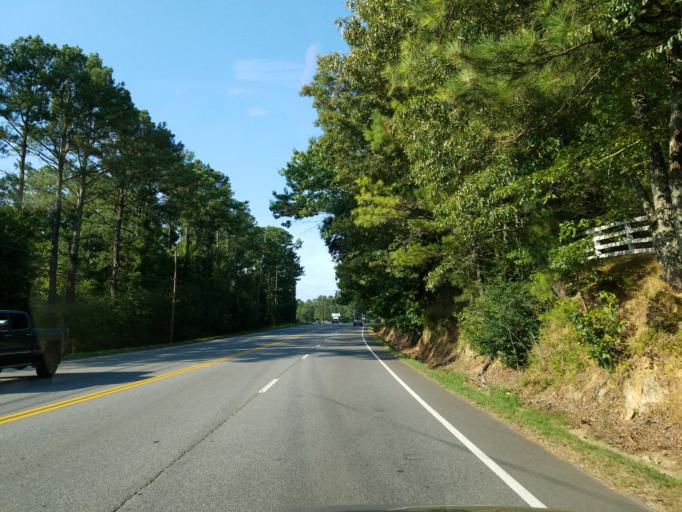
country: US
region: Georgia
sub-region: Bartow County
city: Cartersville
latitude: 34.2296
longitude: -84.7847
